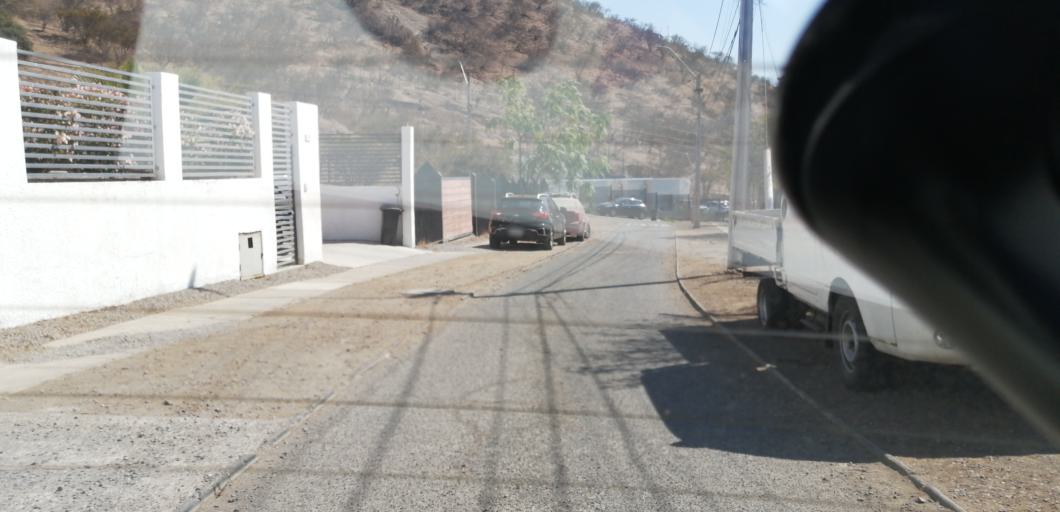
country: CL
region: Santiago Metropolitan
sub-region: Provincia de Santiago
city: Lo Prado
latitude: -33.4535
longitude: -70.8241
